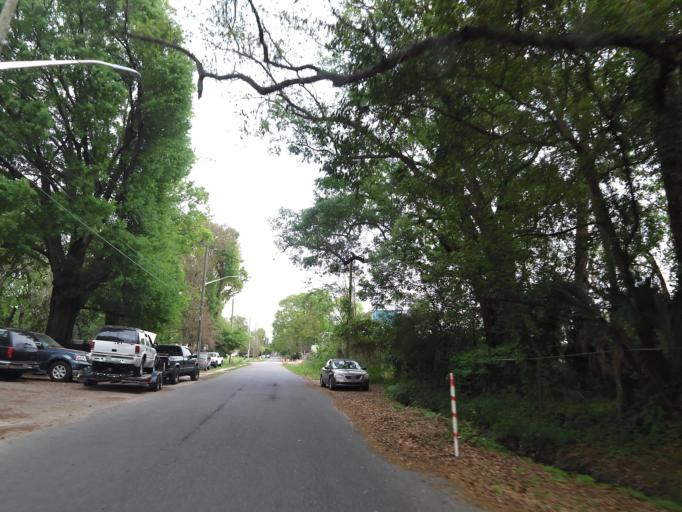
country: US
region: Florida
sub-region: Duval County
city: Jacksonville
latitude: 30.3231
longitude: -81.7275
